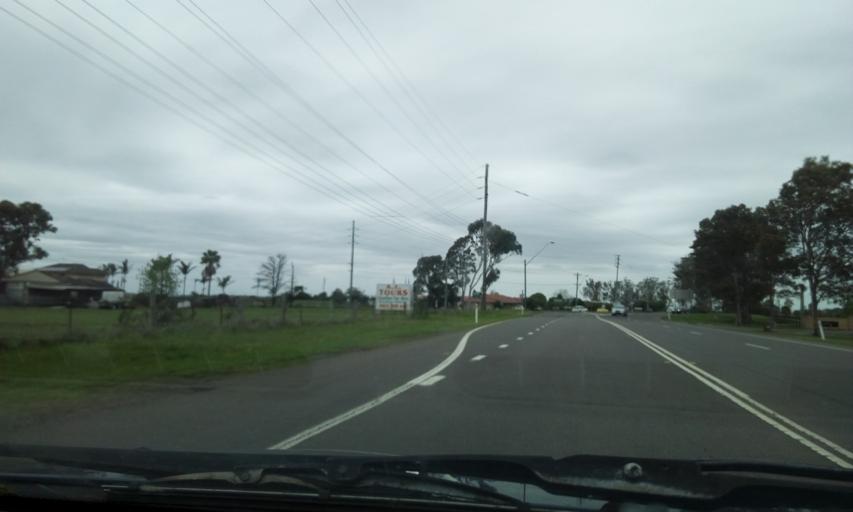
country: AU
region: New South Wales
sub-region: Liverpool
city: Luddenham
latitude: -33.8628
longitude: 150.6981
